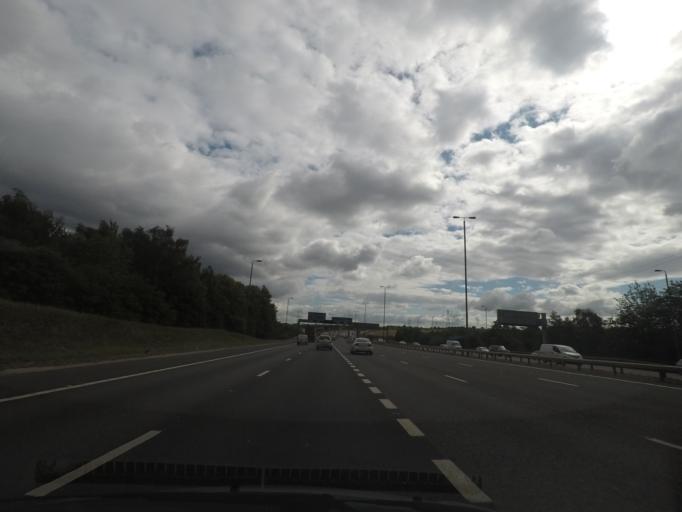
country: GB
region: England
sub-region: City and Borough of Leeds
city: Lofthouse
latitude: 53.7427
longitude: -1.5145
